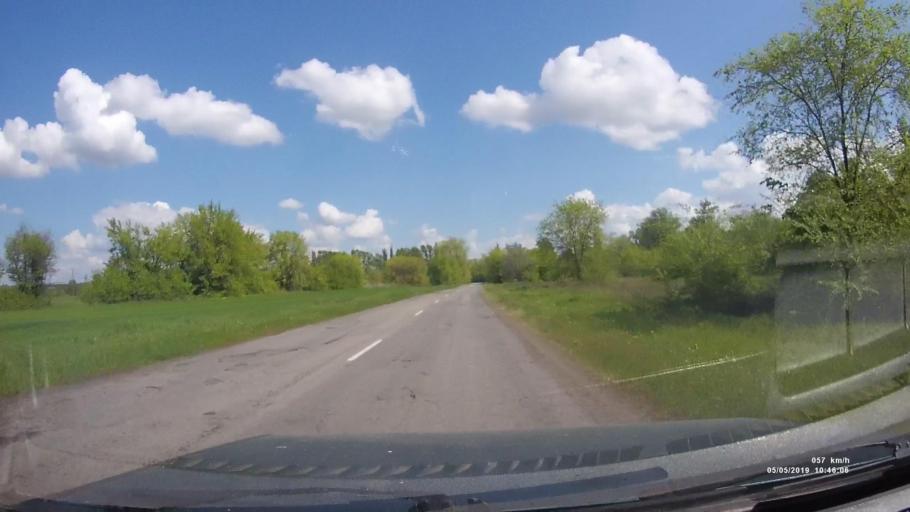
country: RU
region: Rostov
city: Ust'-Donetskiy
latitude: 47.6320
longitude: 40.8417
